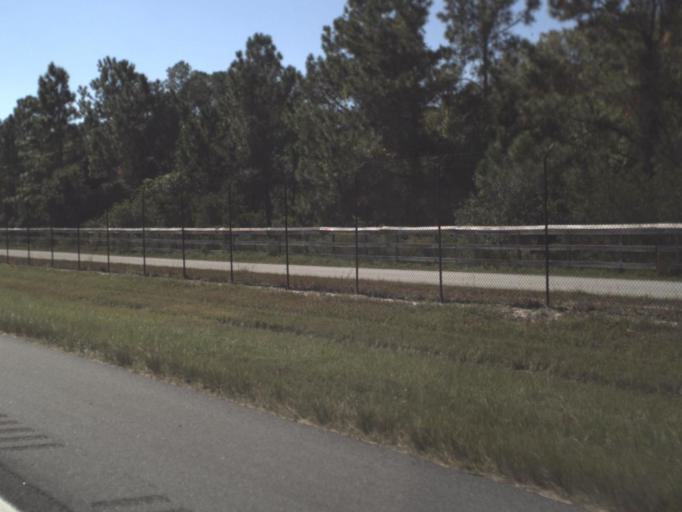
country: US
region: Florida
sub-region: Pasco County
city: Odessa
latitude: 28.2336
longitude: -82.5507
